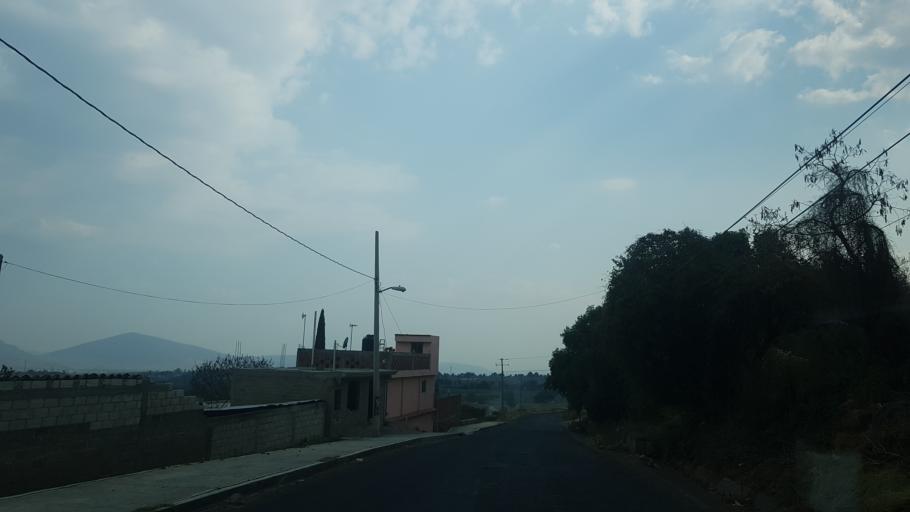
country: MX
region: Puebla
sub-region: Santa Isabel Cholula
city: San Martin Tlamapa
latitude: 18.9703
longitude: -98.3945
